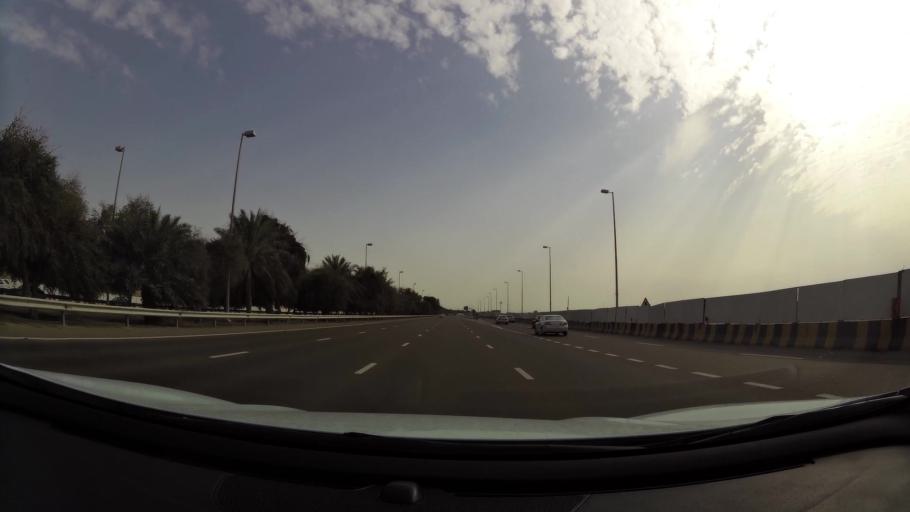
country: AE
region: Abu Dhabi
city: Abu Dhabi
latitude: 24.4291
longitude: 54.6776
